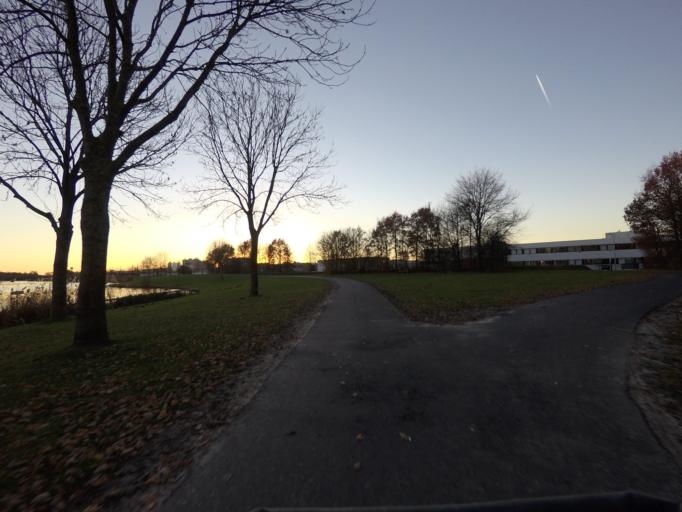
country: NL
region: Utrecht
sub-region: Gemeente Nieuwegein
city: Nieuwegein
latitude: 52.0783
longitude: 5.0594
